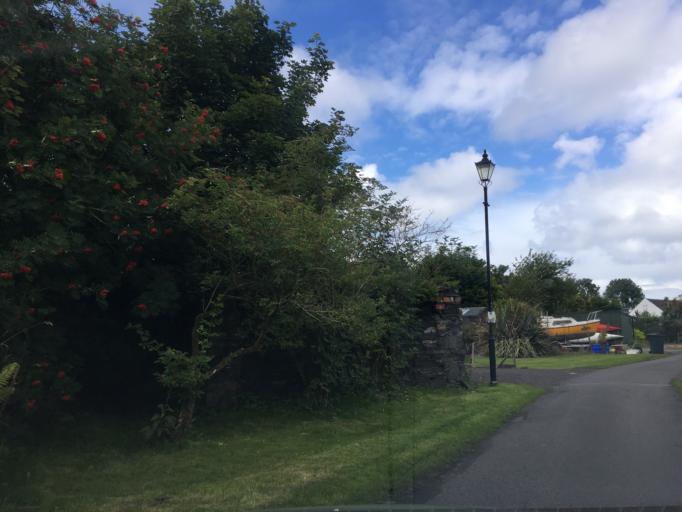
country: GB
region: Scotland
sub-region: Argyll and Bute
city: Oban
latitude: 56.2166
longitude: -5.6308
